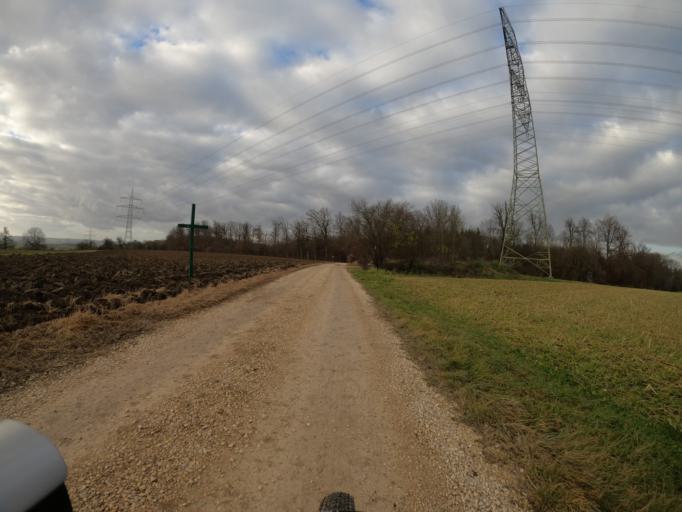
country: DE
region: Baden-Wuerttemberg
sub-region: Regierungsbezirk Stuttgart
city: Notzingen
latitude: 48.6804
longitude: 9.4507
